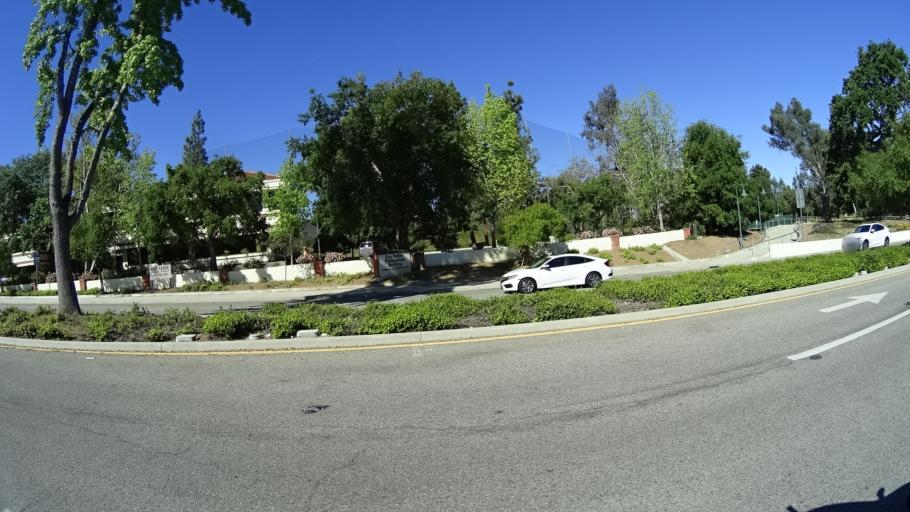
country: US
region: California
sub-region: Ventura County
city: Thousand Oaks
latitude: 34.1762
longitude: -118.8765
